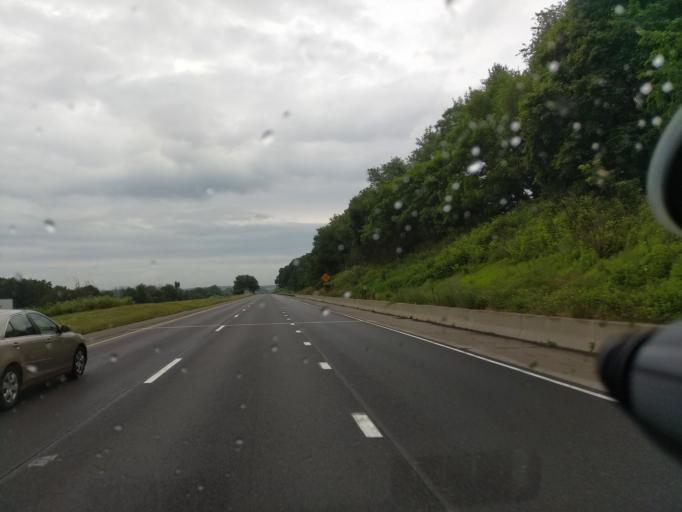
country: US
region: Pennsylvania
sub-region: Northumberland County
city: Milton
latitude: 41.0268
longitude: -76.8018
